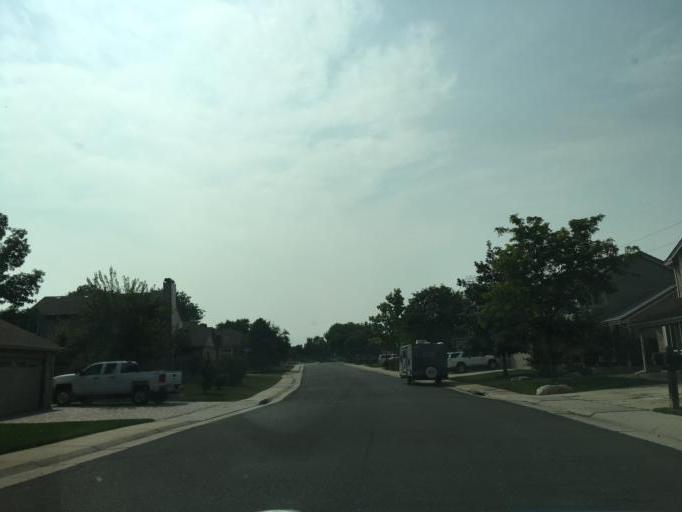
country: US
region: Colorado
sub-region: Jefferson County
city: Arvada
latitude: 39.7974
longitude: -105.1328
